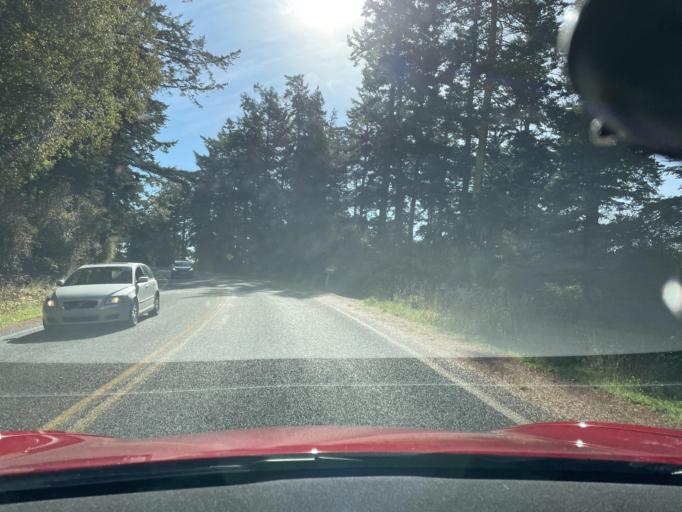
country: US
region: Washington
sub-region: San Juan County
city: Friday Harbor
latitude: 48.4666
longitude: -123.0305
